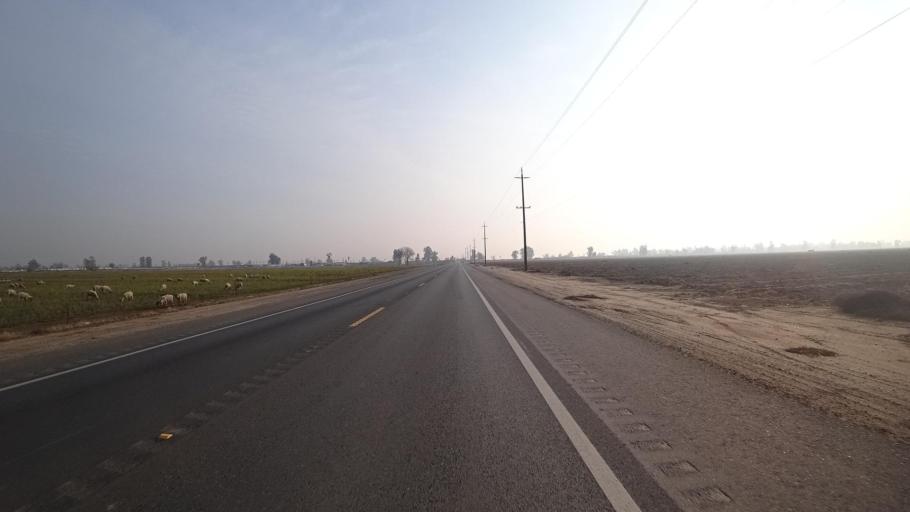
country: US
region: California
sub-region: Kern County
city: Greenfield
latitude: 35.2086
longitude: -119.0191
